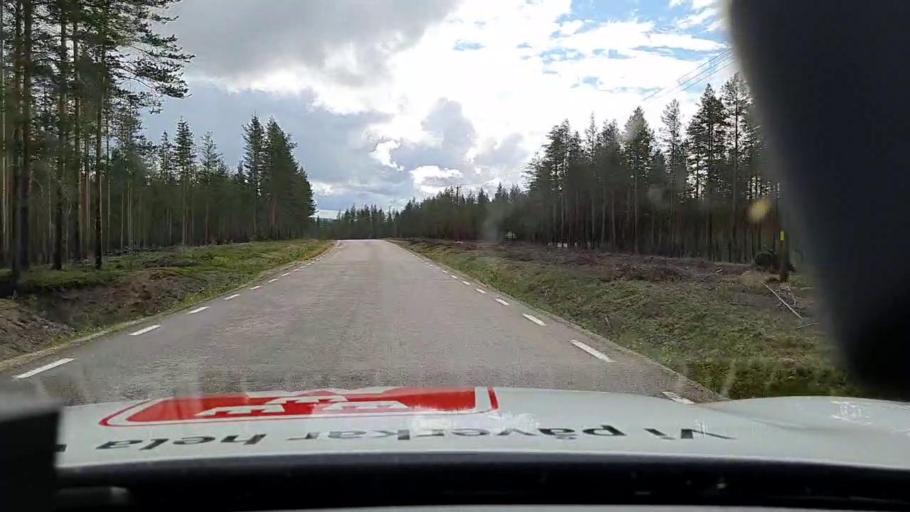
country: SE
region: Norrbotten
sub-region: Overkalix Kommun
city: OEverkalix
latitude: 66.2511
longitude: 22.8778
